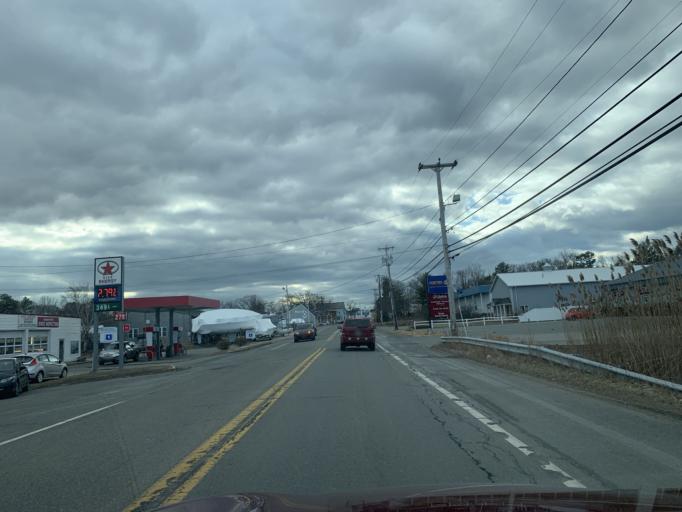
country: US
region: Massachusetts
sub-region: Essex County
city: Newburyport
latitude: 42.8204
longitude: -70.8680
